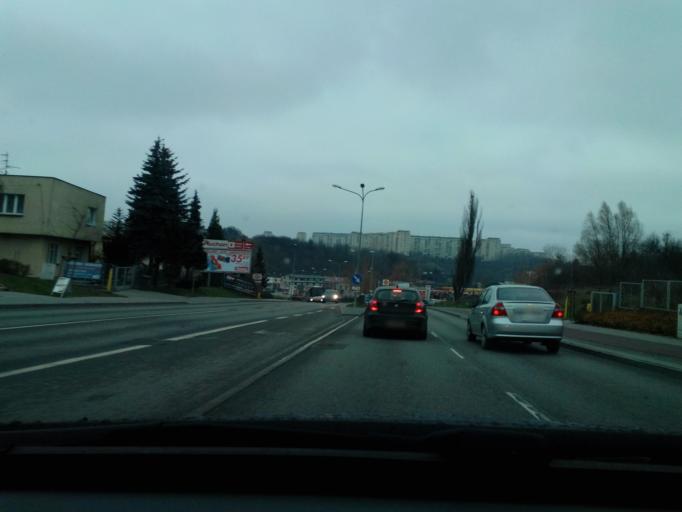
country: PL
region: Pomeranian Voivodeship
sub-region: Gdansk
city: Gdansk
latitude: 54.3446
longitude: 18.6029
